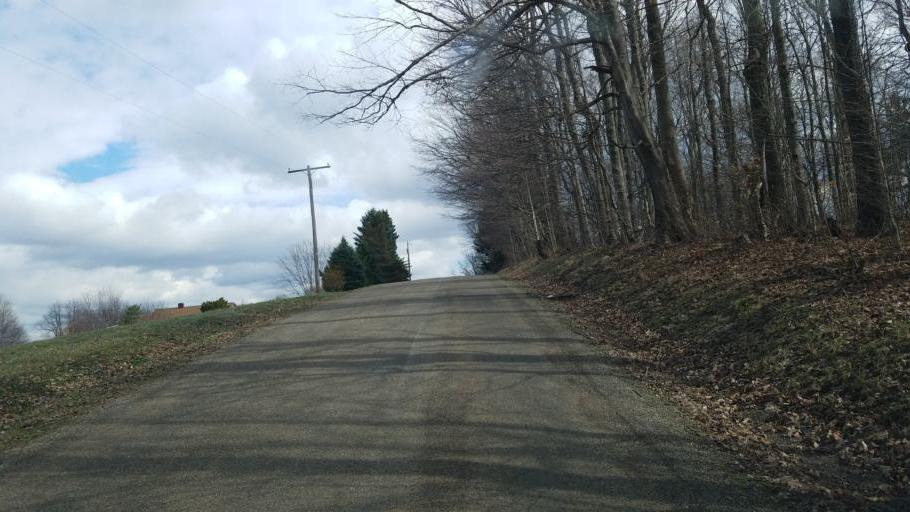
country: US
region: Ohio
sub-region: Sandusky County
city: Bellville
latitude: 40.6529
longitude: -82.4518
